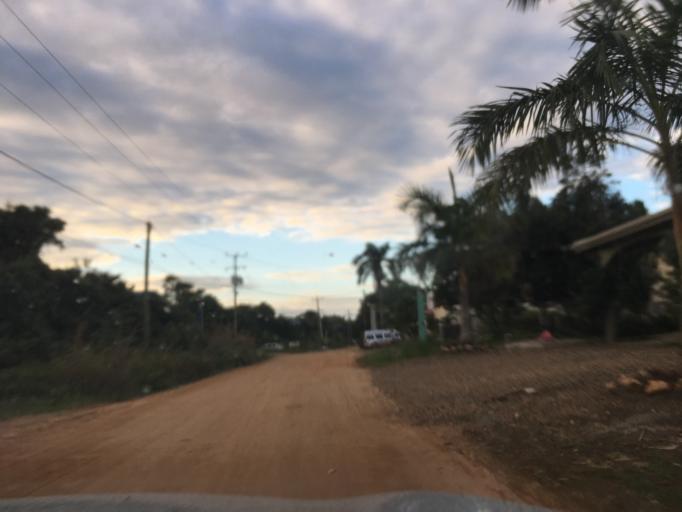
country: BZ
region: Stann Creek
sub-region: Dangriga
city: Dangriga
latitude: 16.8373
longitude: -88.2689
